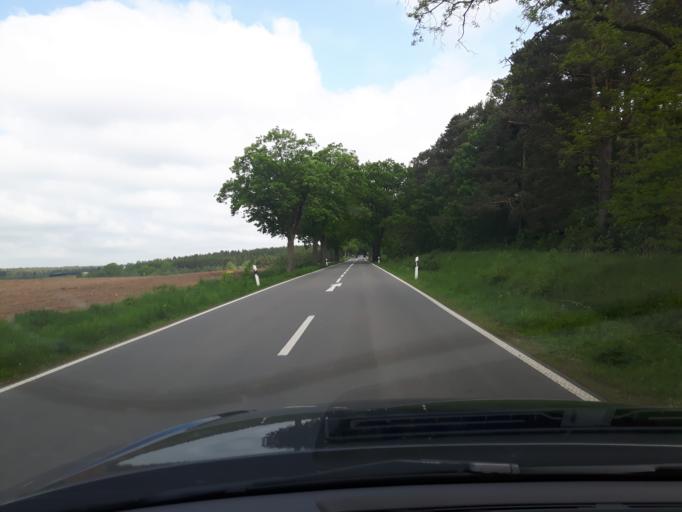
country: DE
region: Mecklenburg-Vorpommern
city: Grabowhofe
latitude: 53.6104
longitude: 12.4668
